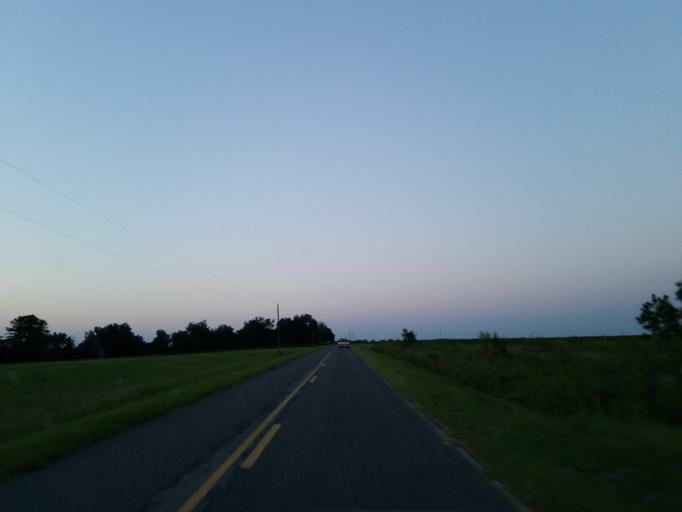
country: US
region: Georgia
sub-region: Dooly County
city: Unadilla
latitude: 32.2706
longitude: -83.7967
